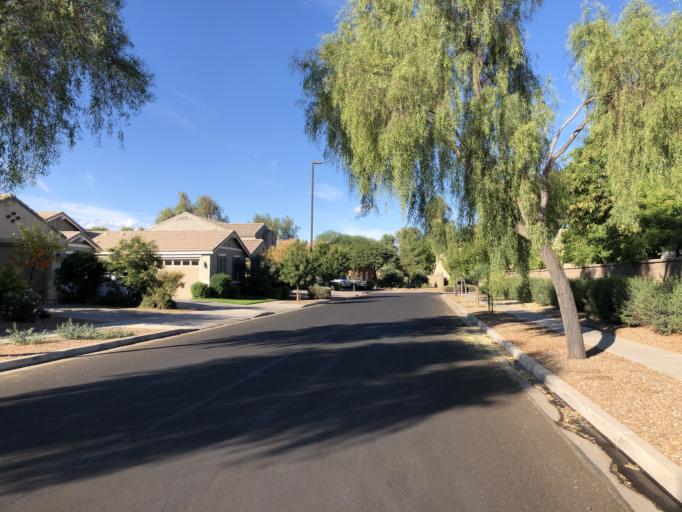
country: US
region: Arizona
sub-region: Maricopa County
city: Queen Creek
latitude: 33.2720
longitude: -111.6890
